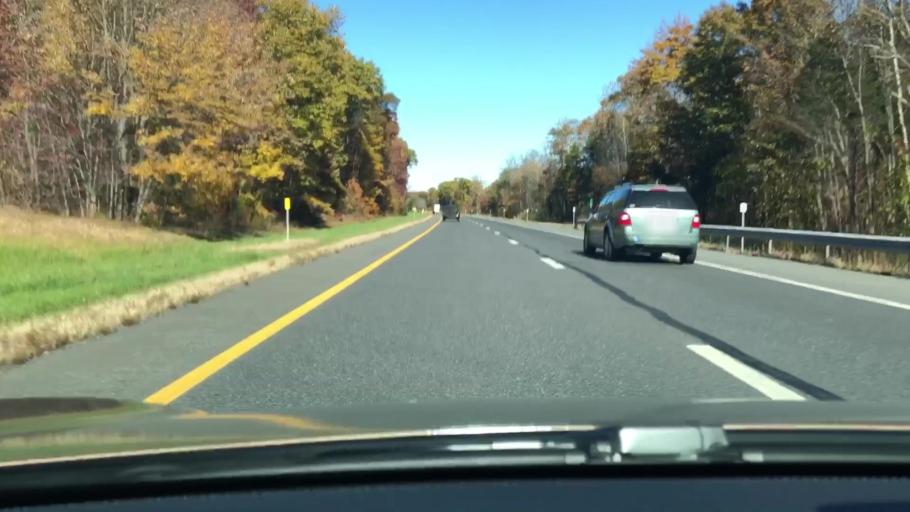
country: US
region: New York
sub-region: Ulster County
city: New Paltz
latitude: 41.7565
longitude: -74.0577
